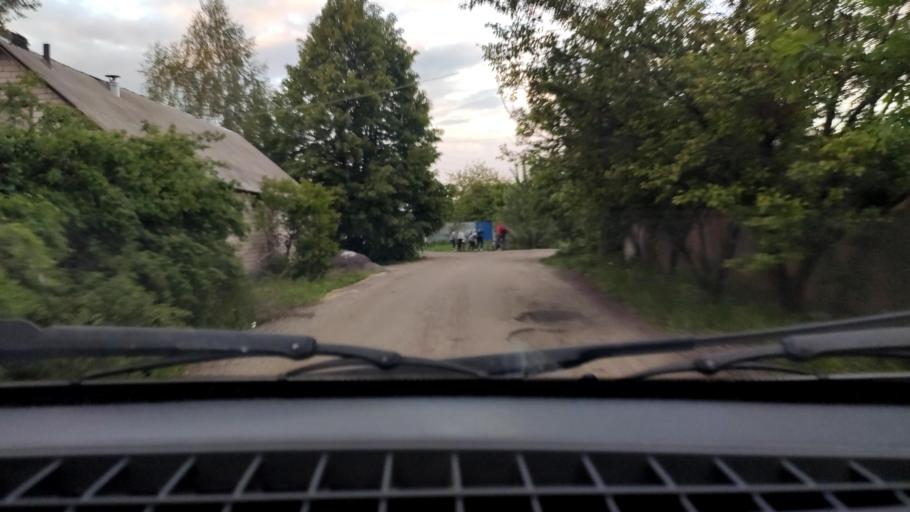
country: RU
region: Voronezj
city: Somovo
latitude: 51.6804
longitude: 39.3247
